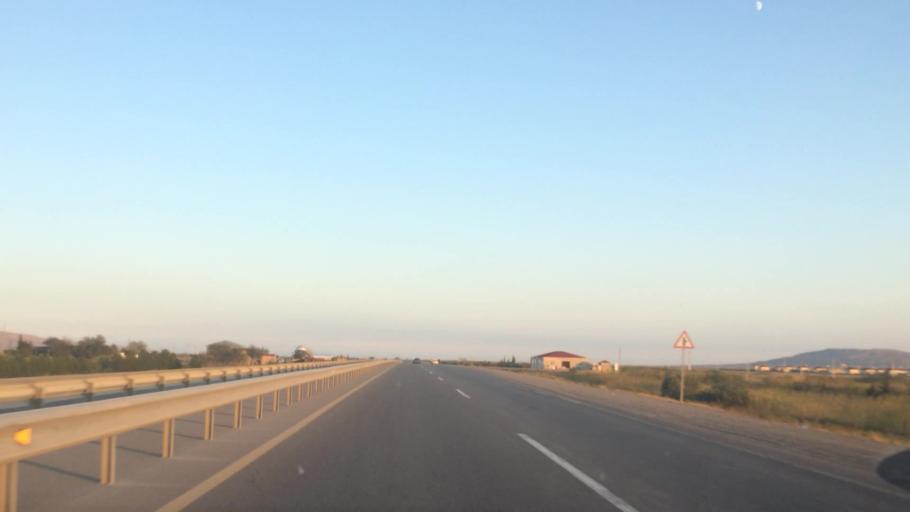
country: AZ
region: Baki
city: Qobustan
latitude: 39.9861
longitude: 49.2083
